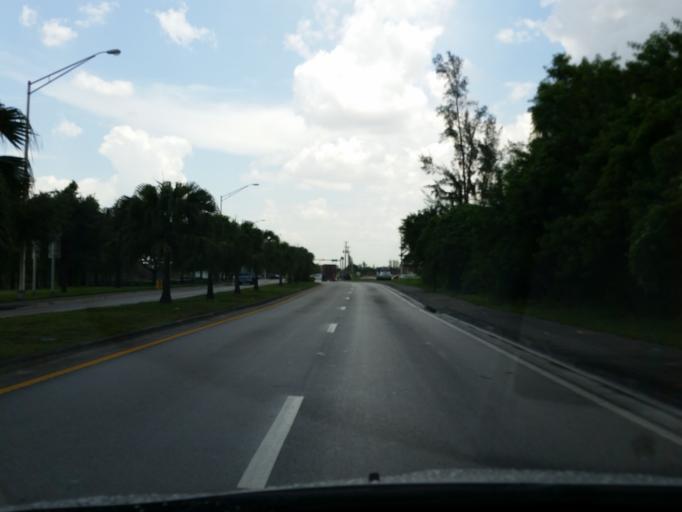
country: US
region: Florida
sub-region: Miami-Dade County
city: Sweetwater
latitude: 25.7844
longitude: -80.3751
